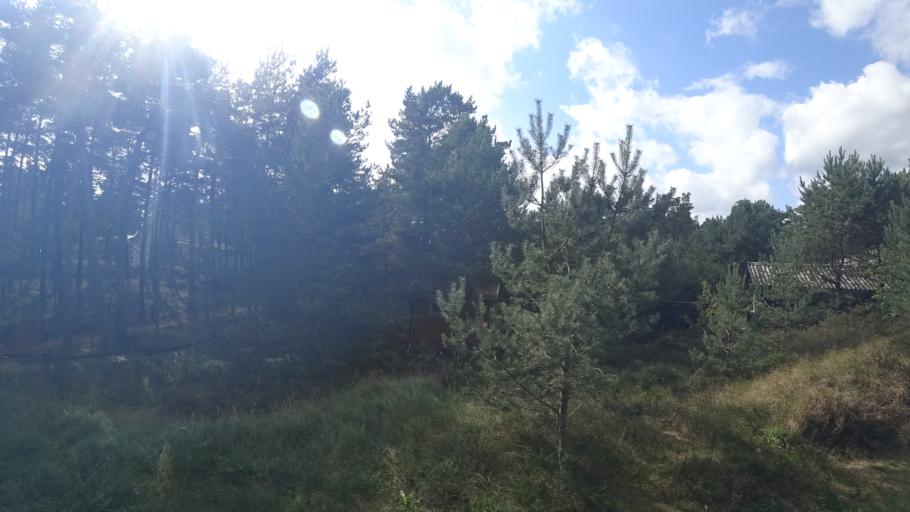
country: SE
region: Skane
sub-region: Kristianstads Kommun
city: Ahus
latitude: 55.9152
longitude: 14.2913
